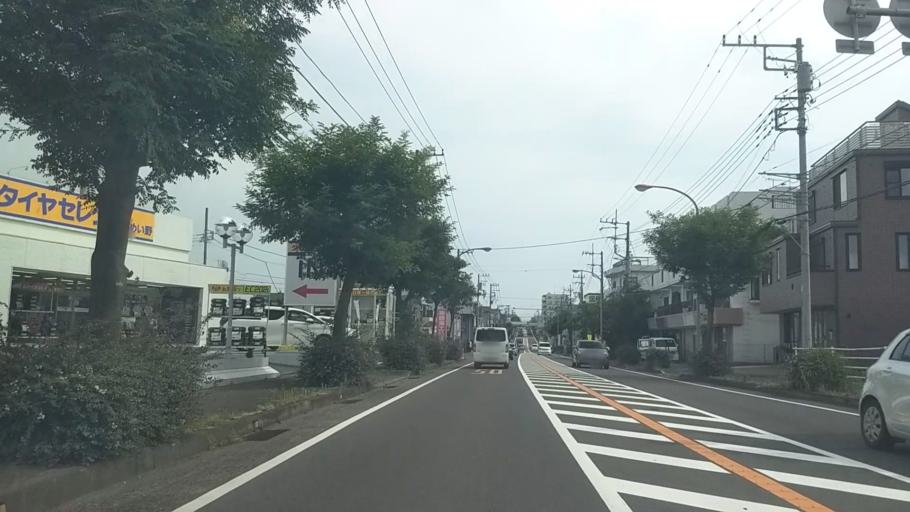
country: JP
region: Kanagawa
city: Fujisawa
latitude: 35.3704
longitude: 139.4790
